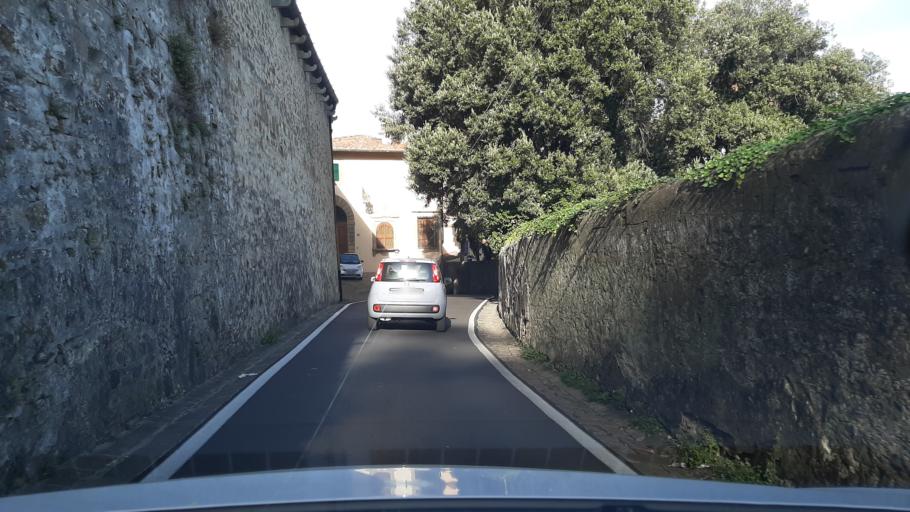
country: IT
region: Tuscany
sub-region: Province of Florence
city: Florence
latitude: 43.7517
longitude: 11.2550
